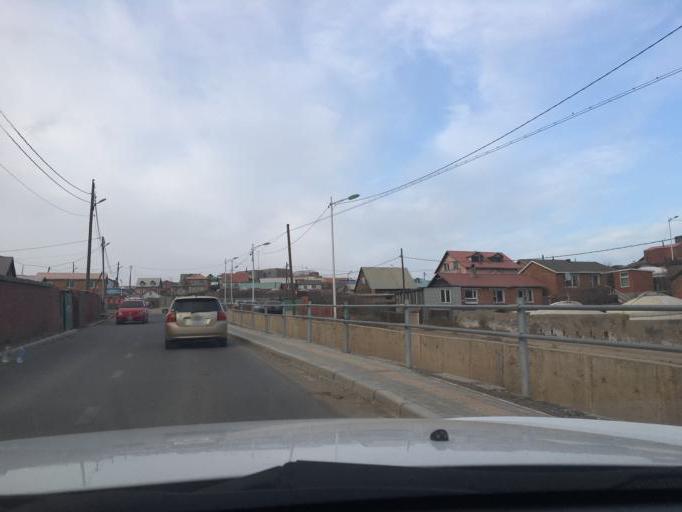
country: MN
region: Ulaanbaatar
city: Ulaanbaatar
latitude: 47.9216
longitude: 106.8525
